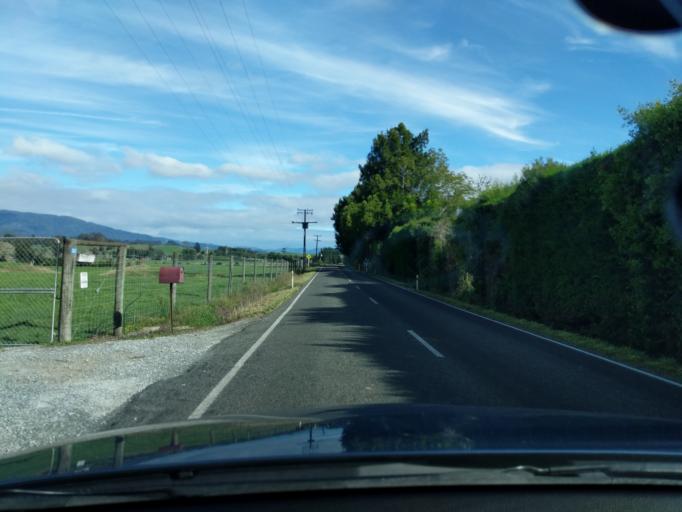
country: NZ
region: Tasman
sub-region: Tasman District
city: Takaka
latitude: -40.8515
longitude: 172.8432
